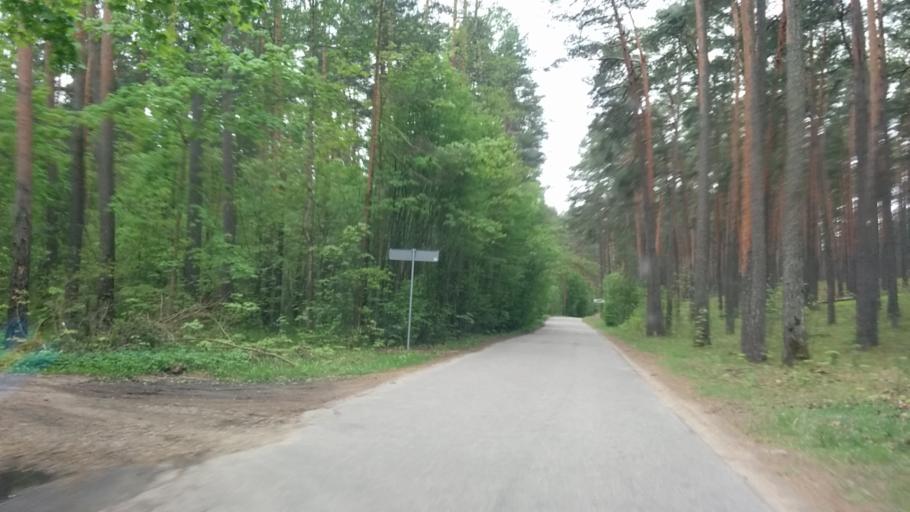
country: LV
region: Babite
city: Pinki
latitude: 56.9444
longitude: 23.9453
